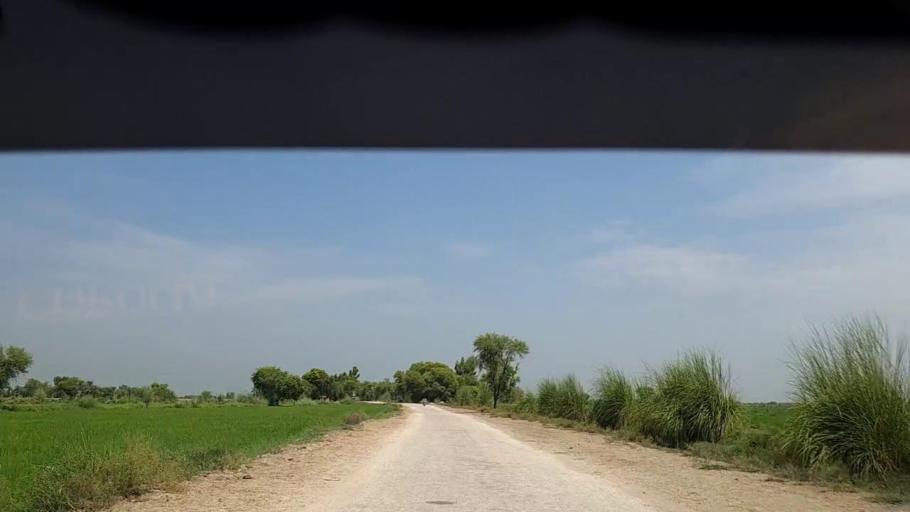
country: PK
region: Sindh
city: Shikarpur
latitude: 28.0656
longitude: 68.7052
